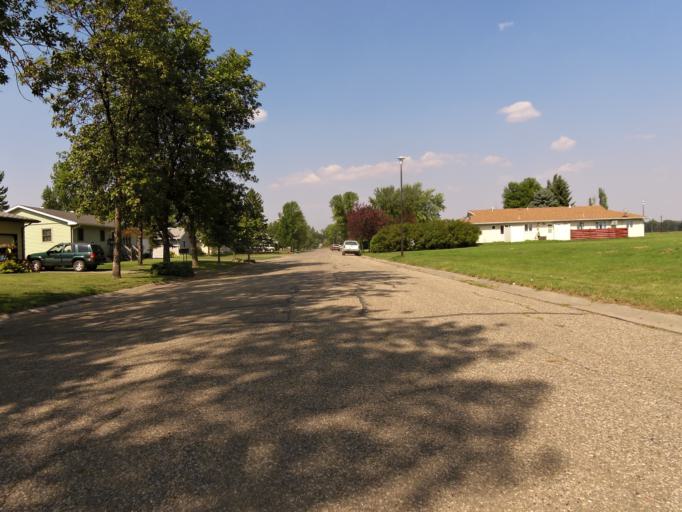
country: US
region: North Dakota
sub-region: Walsh County
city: Grafton
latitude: 48.4157
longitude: -97.3981
